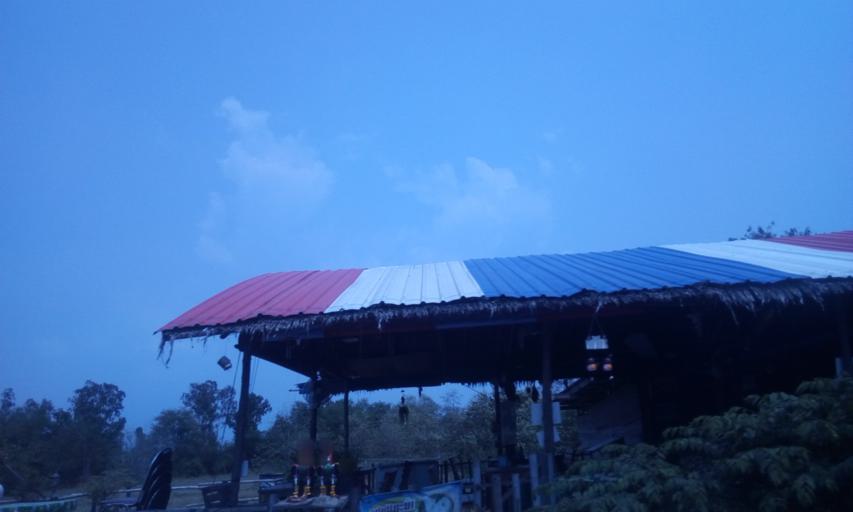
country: TH
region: Chon Buri
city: Phanat Nikhom
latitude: 13.4632
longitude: 101.1728
